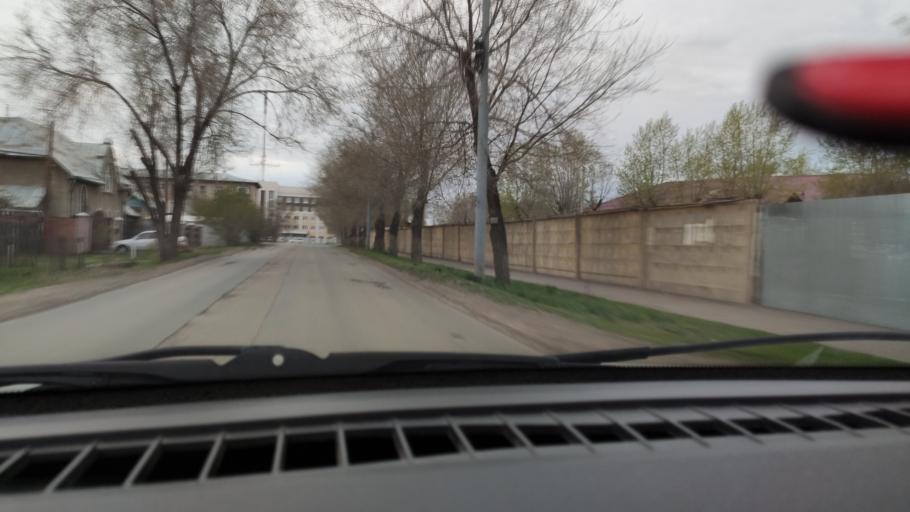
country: RU
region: Orenburg
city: Orenburg
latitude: 51.7759
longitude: 55.1261
